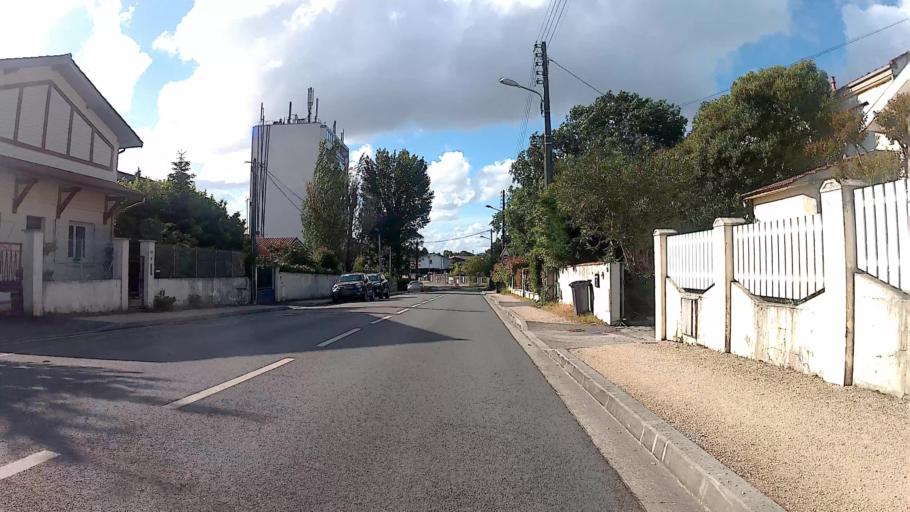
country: FR
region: Aquitaine
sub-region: Departement de la Gironde
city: Pessac
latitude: 44.8148
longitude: -0.6226
